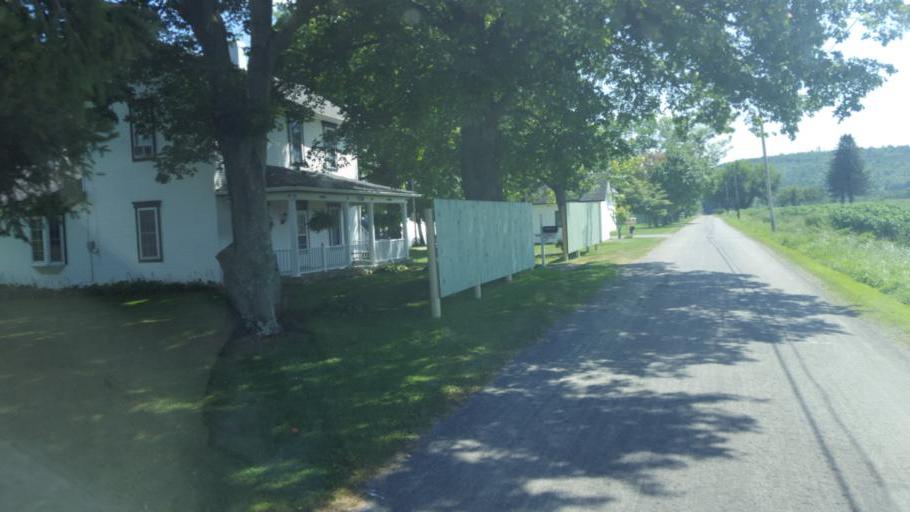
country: US
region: Pennsylvania
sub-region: Clarion County
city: Knox
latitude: 41.1209
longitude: -79.5486
